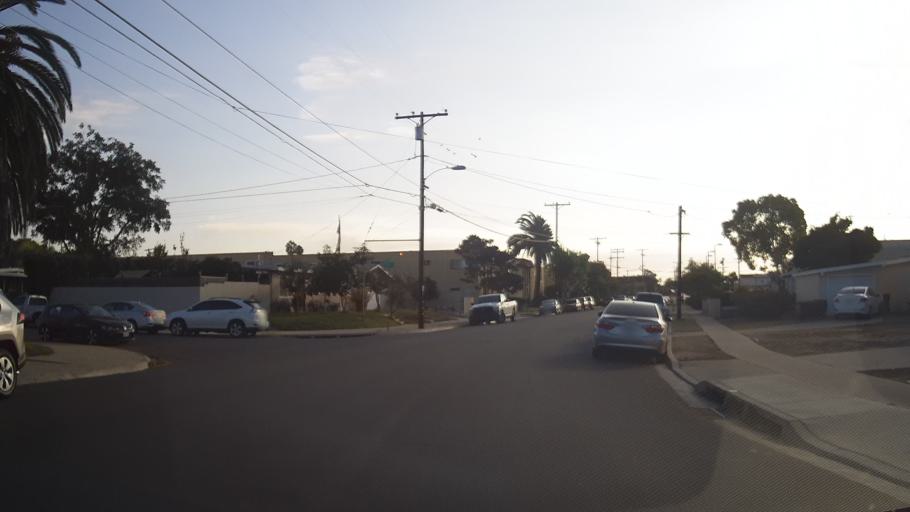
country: US
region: California
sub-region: San Diego County
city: La Jolla
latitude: 32.8360
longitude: -117.1891
